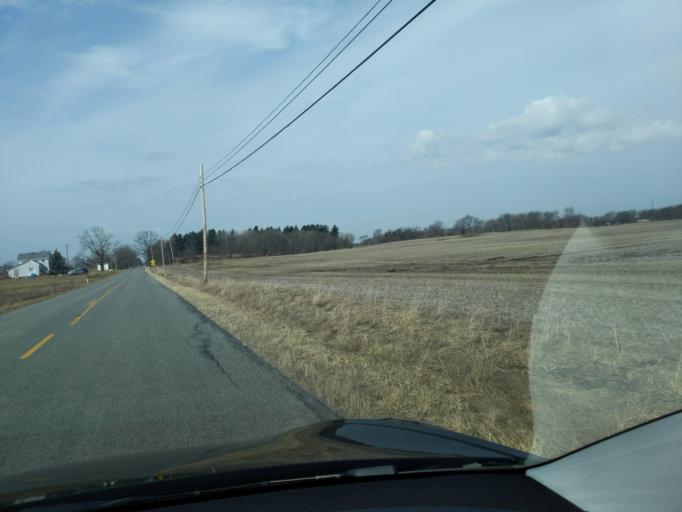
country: US
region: Michigan
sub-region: Ingham County
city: Williamston
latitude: 42.6587
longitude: -84.3227
